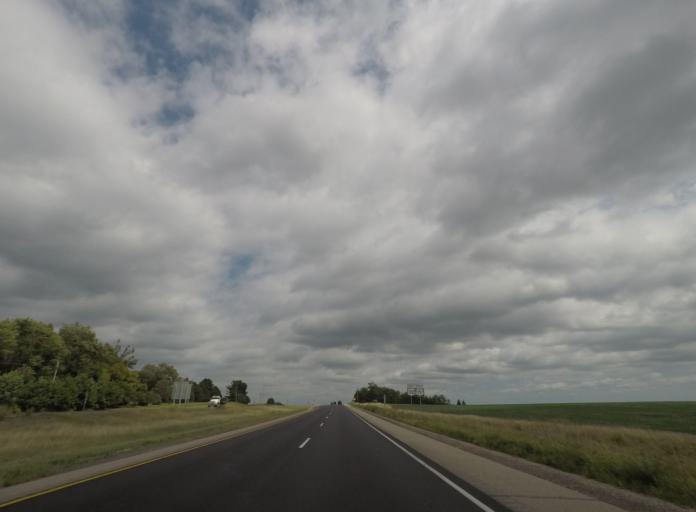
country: US
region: Iowa
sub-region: Linn County
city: Ely
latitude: 41.9264
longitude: -91.6275
